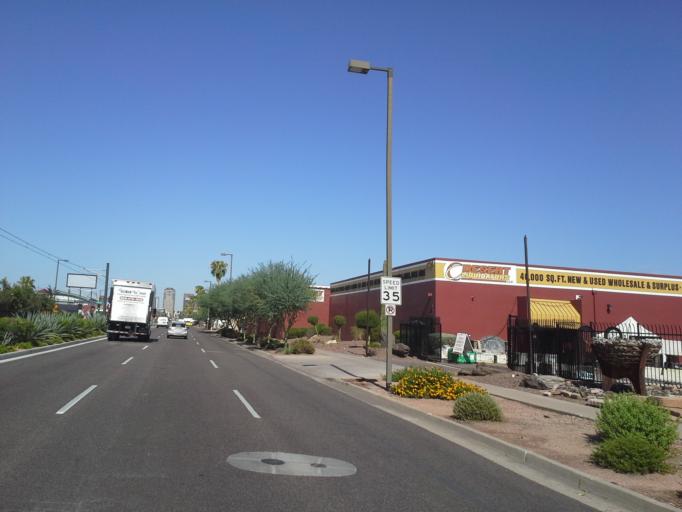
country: US
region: Arizona
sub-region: Maricopa County
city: Phoenix
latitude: 33.4484
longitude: -112.0441
